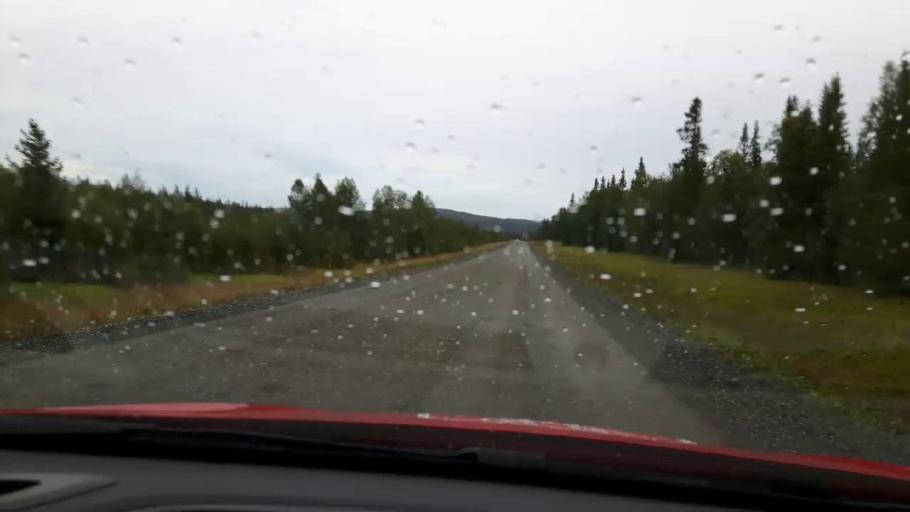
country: NO
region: Nord-Trondelag
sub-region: Meraker
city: Meraker
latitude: 63.5589
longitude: 12.3076
